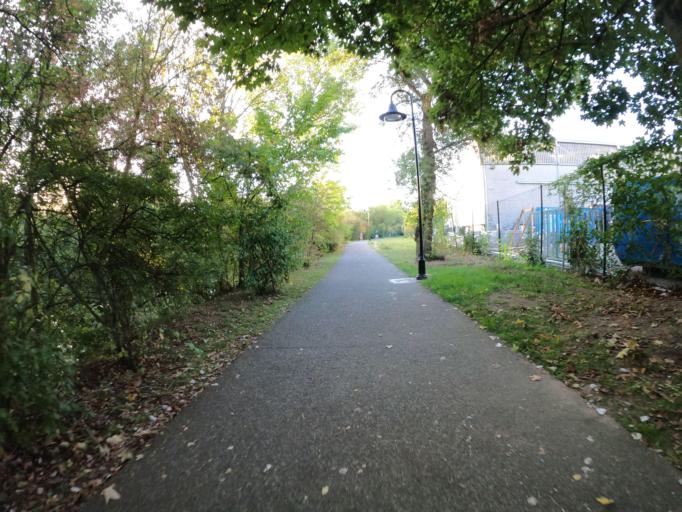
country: ES
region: Navarre
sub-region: Provincia de Navarra
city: Baranain
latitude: 42.8119
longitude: -1.6818
